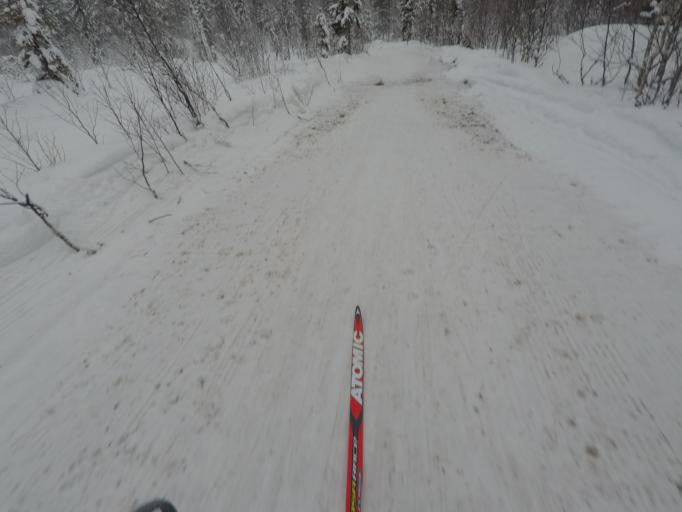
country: SE
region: Vaermland
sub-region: Filipstads Kommun
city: Lesjofors
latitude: 60.1618
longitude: 14.4509
